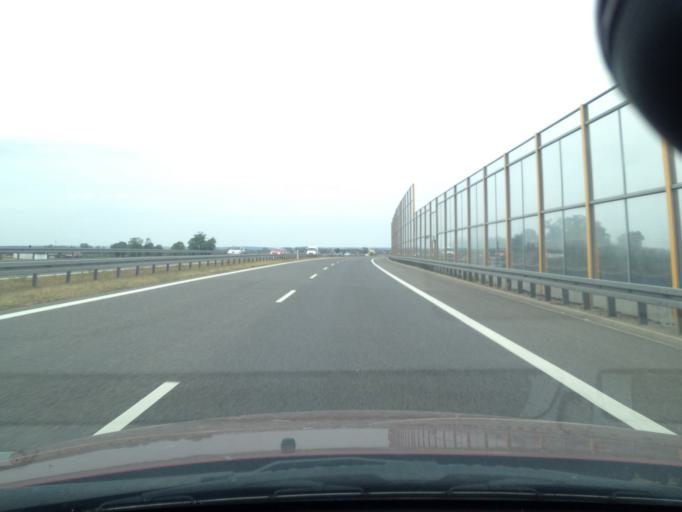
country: PL
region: Lubusz
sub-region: Powiat gorzowski
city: Deszczno
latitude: 52.6691
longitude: 15.3087
